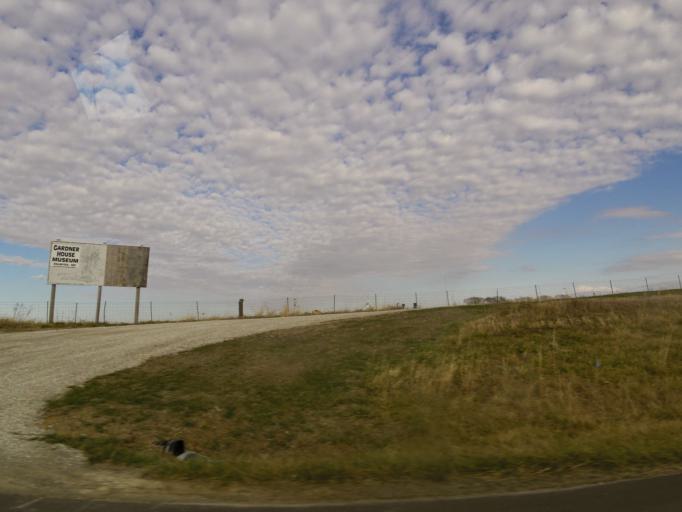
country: US
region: Missouri
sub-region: Marion County
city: Palmyra
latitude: 39.7464
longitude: -91.5144
